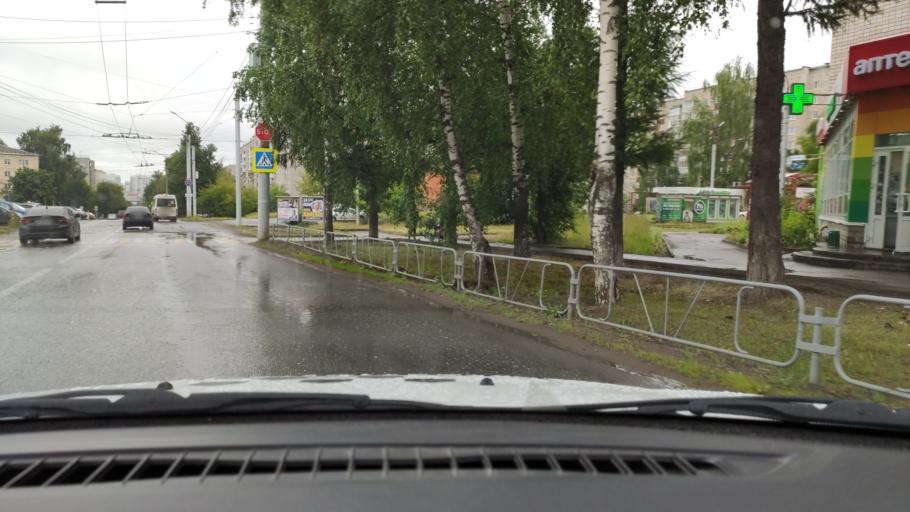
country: RU
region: Udmurtiya
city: Izhevsk
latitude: 56.8764
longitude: 53.1836
